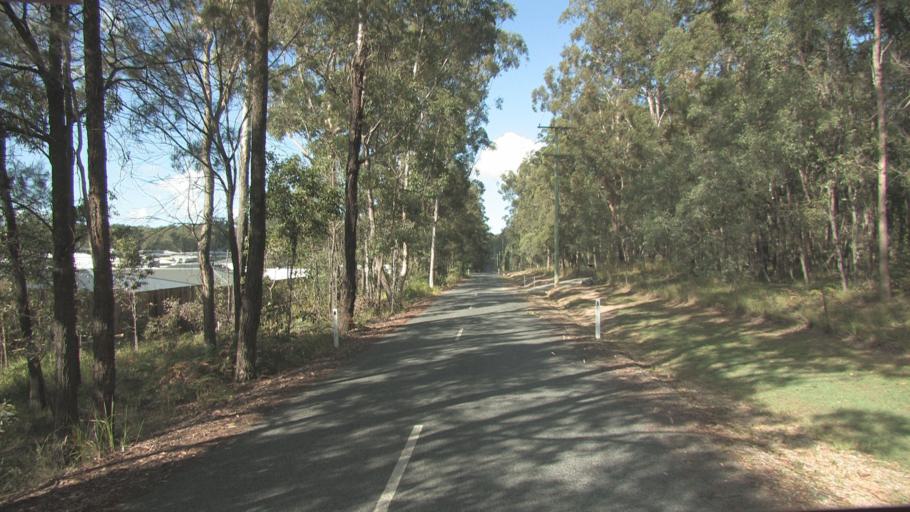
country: AU
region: Queensland
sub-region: Redland
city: Redland Bay
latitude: -27.6531
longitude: 153.2561
